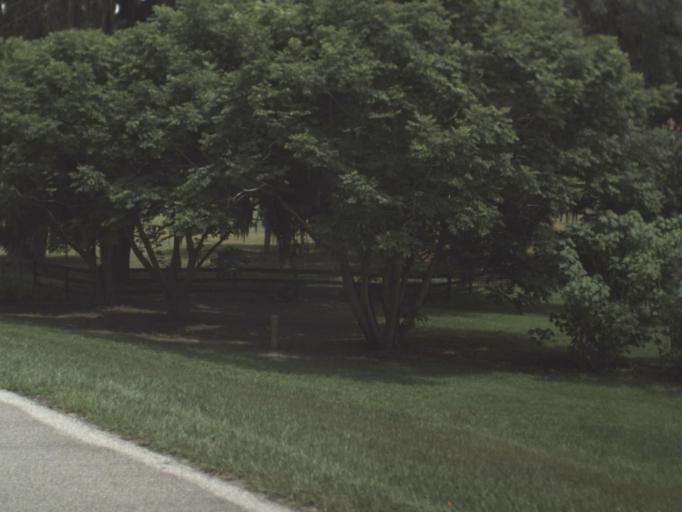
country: US
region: Florida
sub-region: Madison County
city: Madison
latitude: 30.4722
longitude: -83.3124
